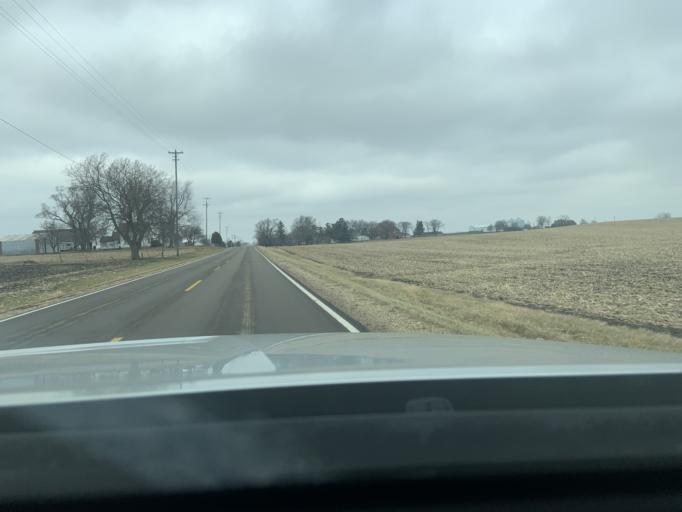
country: US
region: Illinois
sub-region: LaSalle County
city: Seneca
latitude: 41.3942
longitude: -88.6137
